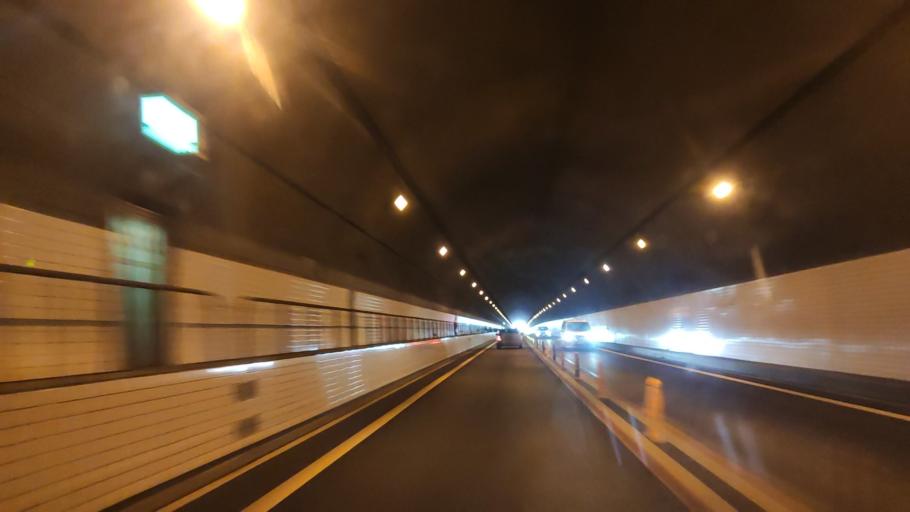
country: JP
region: Tokushima
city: Ikedacho
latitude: 34.0211
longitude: 133.8054
